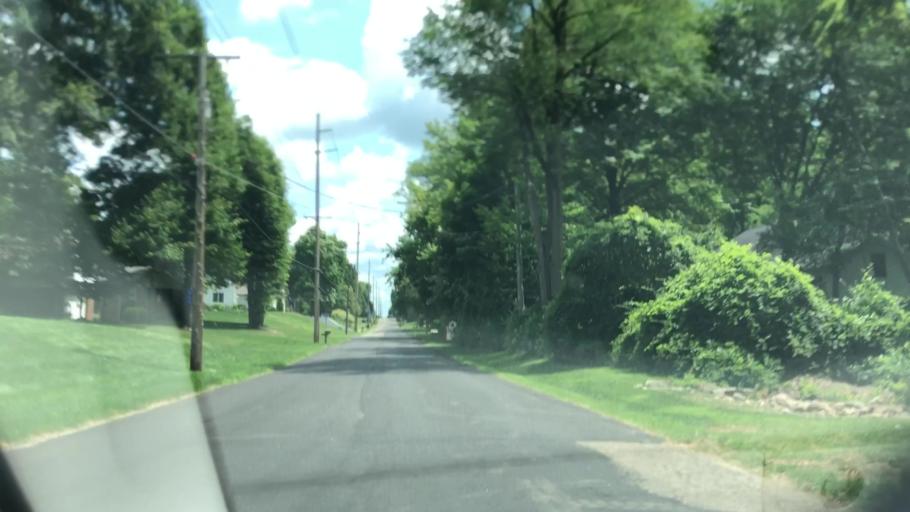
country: US
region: Ohio
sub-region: Stark County
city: Massillon
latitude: 40.8212
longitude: -81.5122
